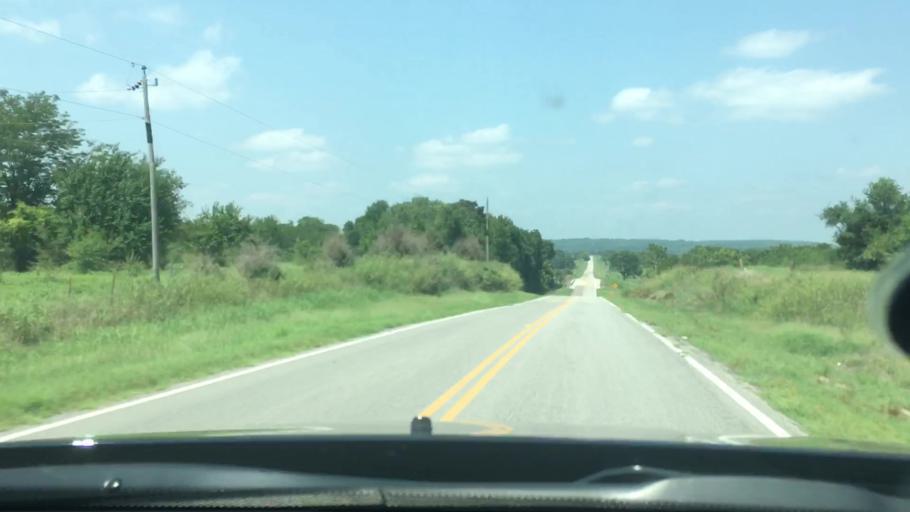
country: US
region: Oklahoma
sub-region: Johnston County
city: Tishomingo
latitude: 34.3863
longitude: -96.4962
